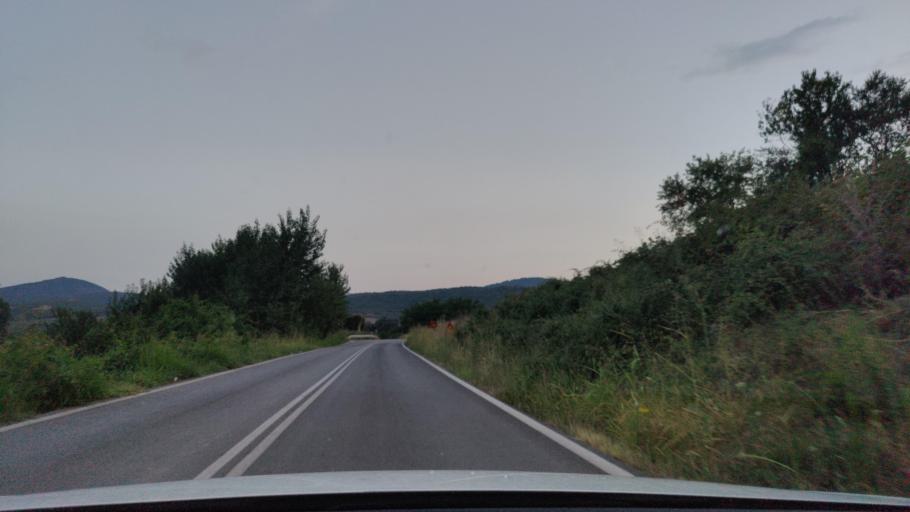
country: GR
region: Central Macedonia
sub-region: Nomos Serron
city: Chrysochorafa
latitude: 41.1403
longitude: 23.2281
